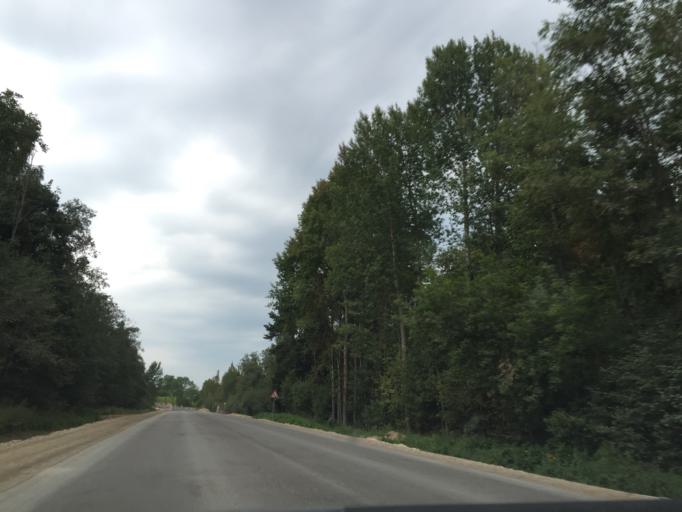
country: LV
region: Ludzas Rajons
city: Ludza
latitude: 56.5362
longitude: 27.6473
